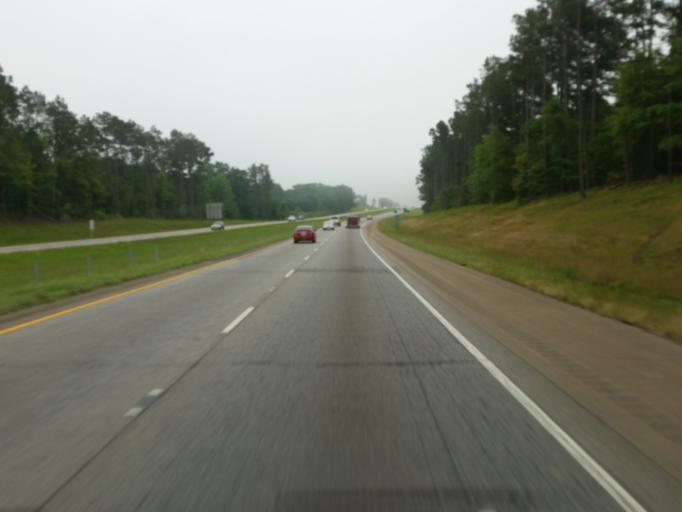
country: US
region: Louisiana
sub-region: Webster Parish
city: Minden
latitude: 32.5876
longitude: -93.2836
